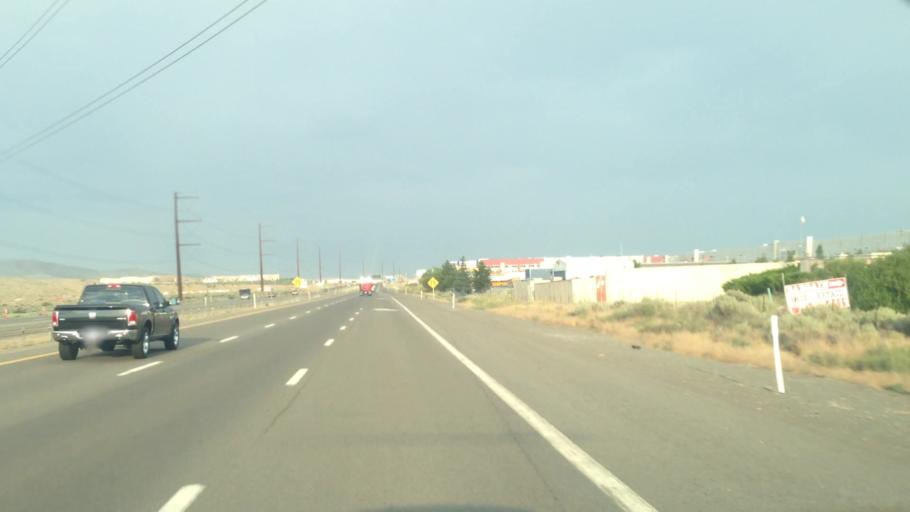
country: US
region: Nevada
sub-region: Washoe County
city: Lemmon Valley
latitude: 39.6171
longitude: -119.8730
